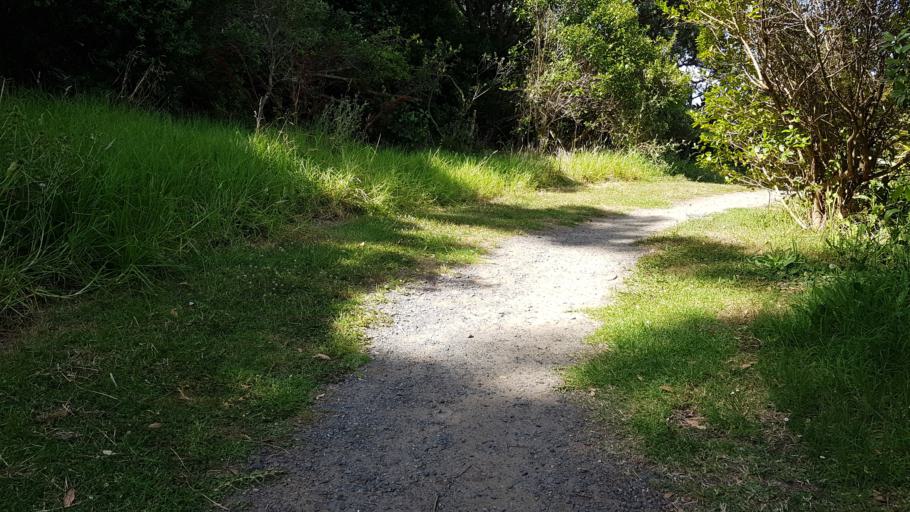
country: NZ
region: Auckland
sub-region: Auckland
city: Rothesay Bay
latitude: -36.6799
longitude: 174.7471
